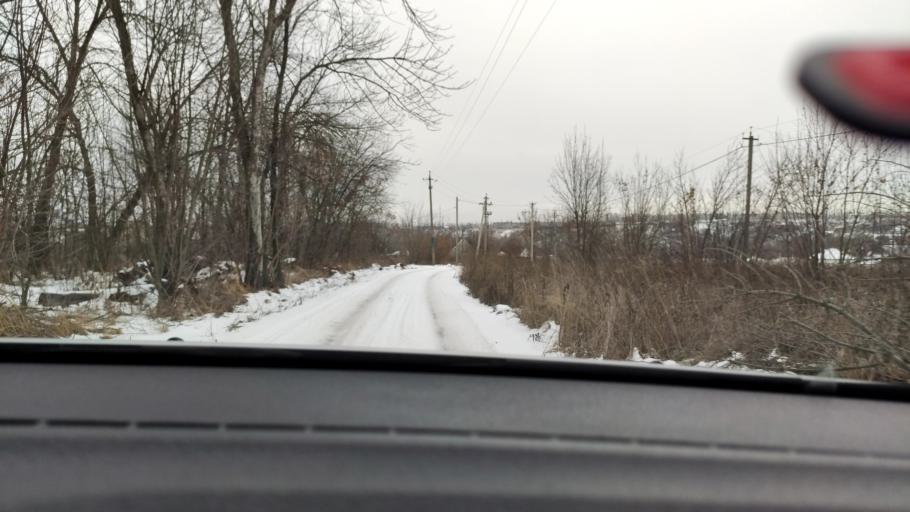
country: RU
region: Voronezj
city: Semiluki
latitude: 51.7028
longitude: 38.9904
